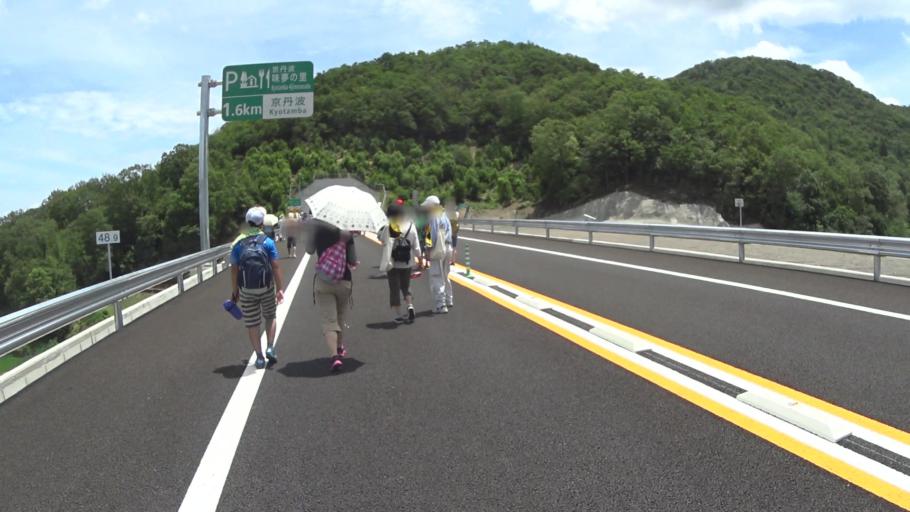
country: JP
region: Kyoto
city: Ayabe
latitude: 35.1605
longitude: 135.3955
